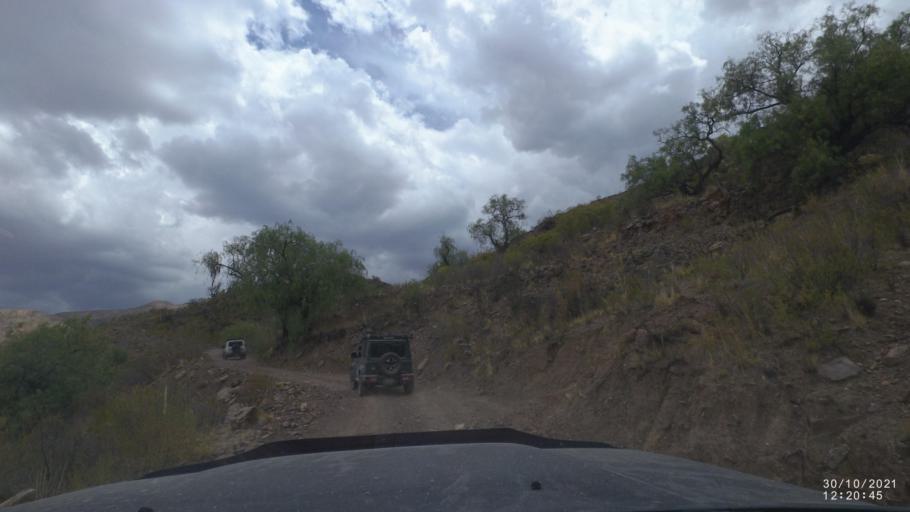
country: BO
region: Cochabamba
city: Colchani
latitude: -17.5701
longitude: -66.6320
